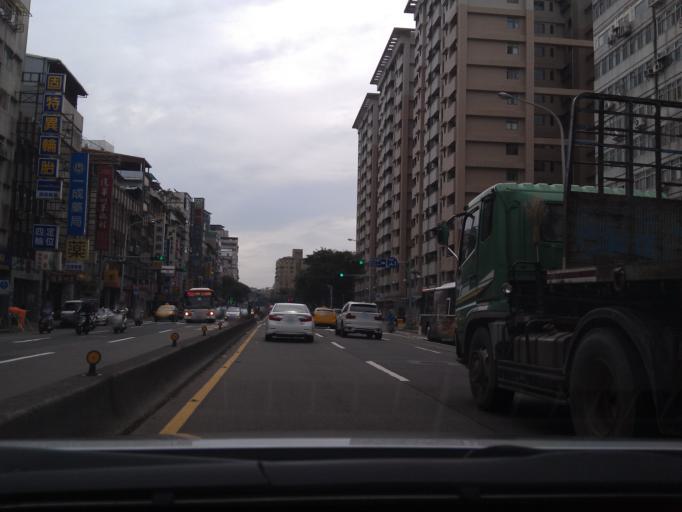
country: TW
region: Taipei
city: Taipei
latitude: 25.0293
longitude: 121.5015
